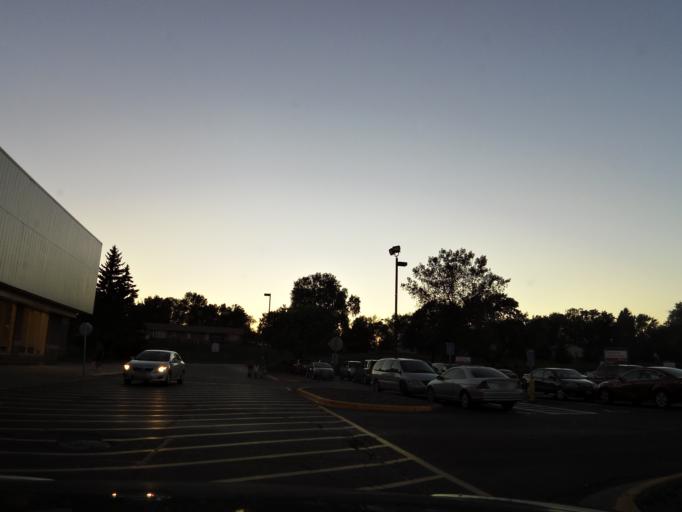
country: US
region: Minnesota
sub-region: Washington County
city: Oakdale
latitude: 44.9606
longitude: -92.9632
